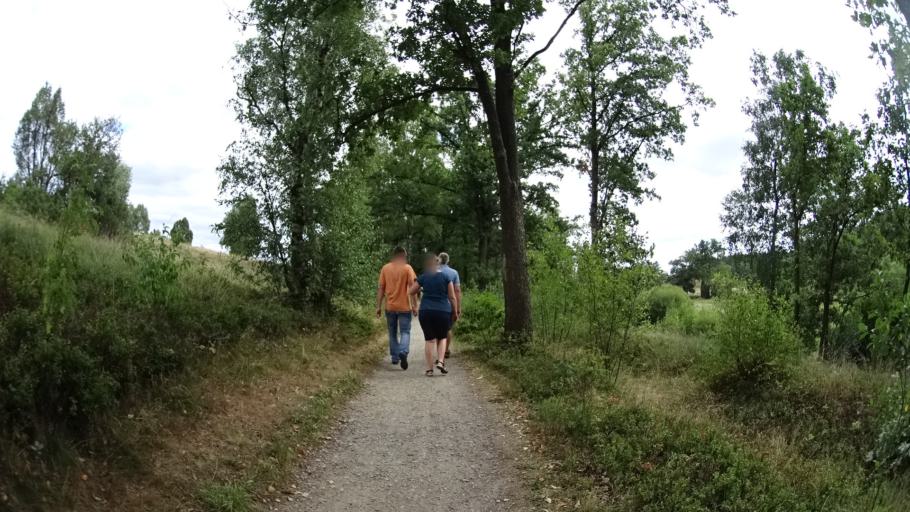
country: DE
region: Lower Saxony
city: Undeloh
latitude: 53.1907
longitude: 9.9803
